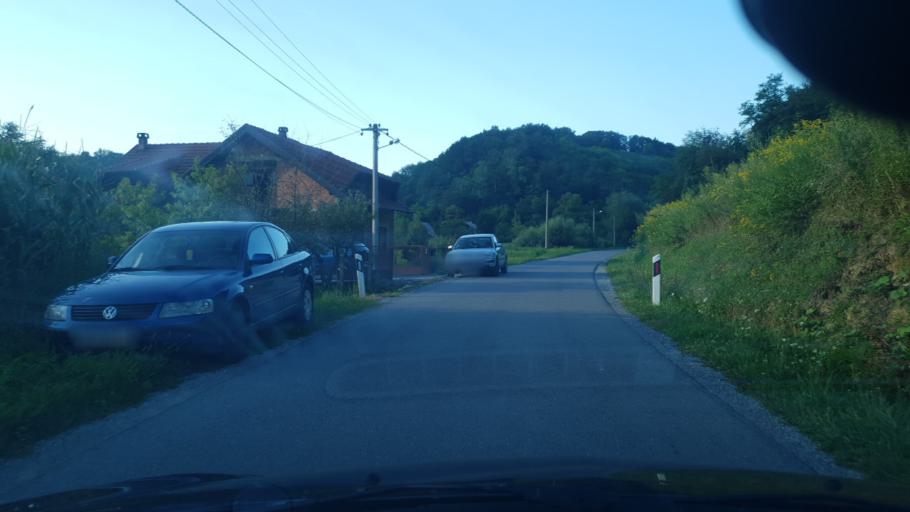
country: HR
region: Krapinsko-Zagorska
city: Zabok
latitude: 46.0487
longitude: 15.8872
